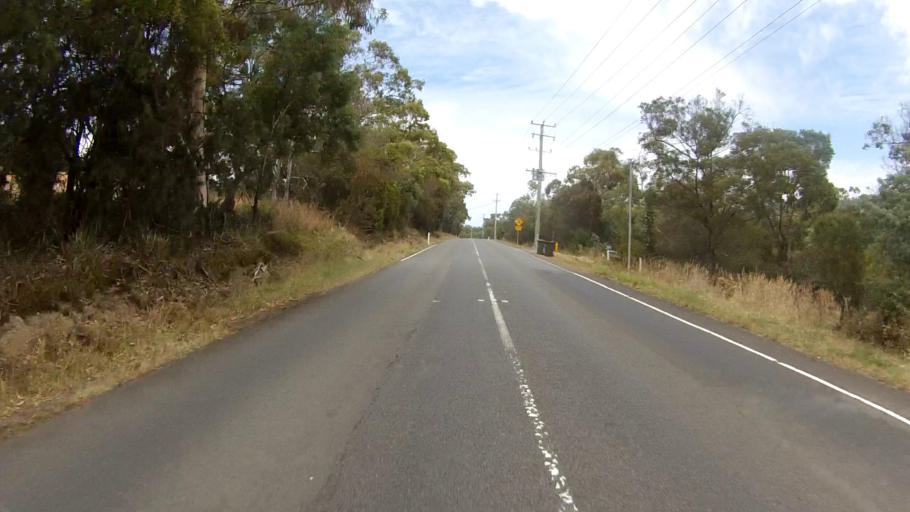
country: AU
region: Tasmania
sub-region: Clarence
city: Acton Park
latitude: -42.8706
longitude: 147.4835
